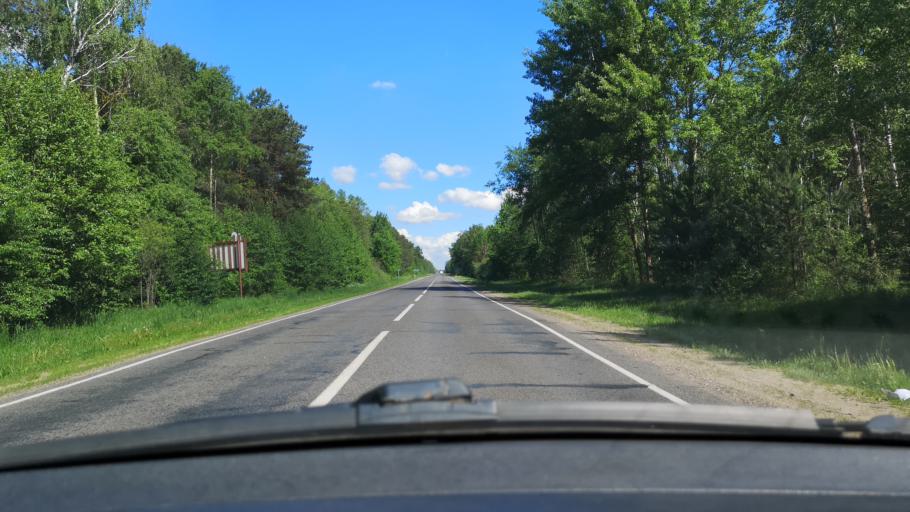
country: BY
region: Brest
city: Brest
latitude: 52.0250
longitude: 23.7300
